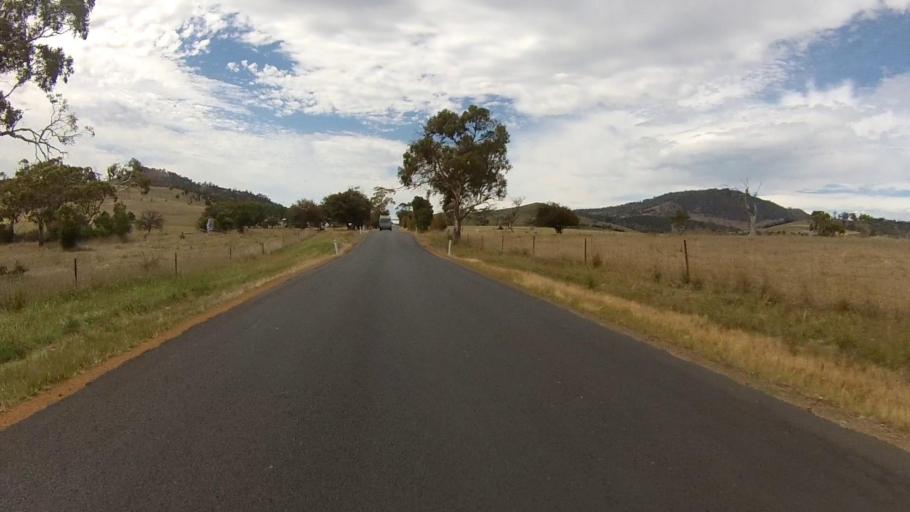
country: AU
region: Tasmania
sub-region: Brighton
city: Old Beach
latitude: -42.7159
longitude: 147.3244
